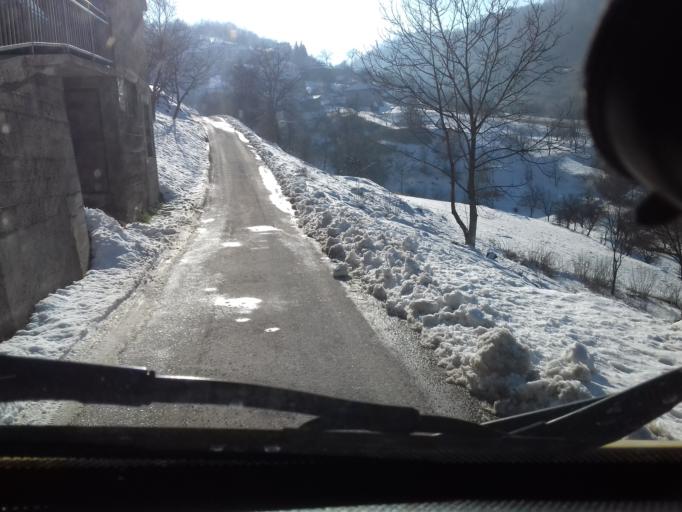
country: BA
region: Federation of Bosnia and Herzegovina
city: Zenica
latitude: 44.1811
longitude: 17.8835
